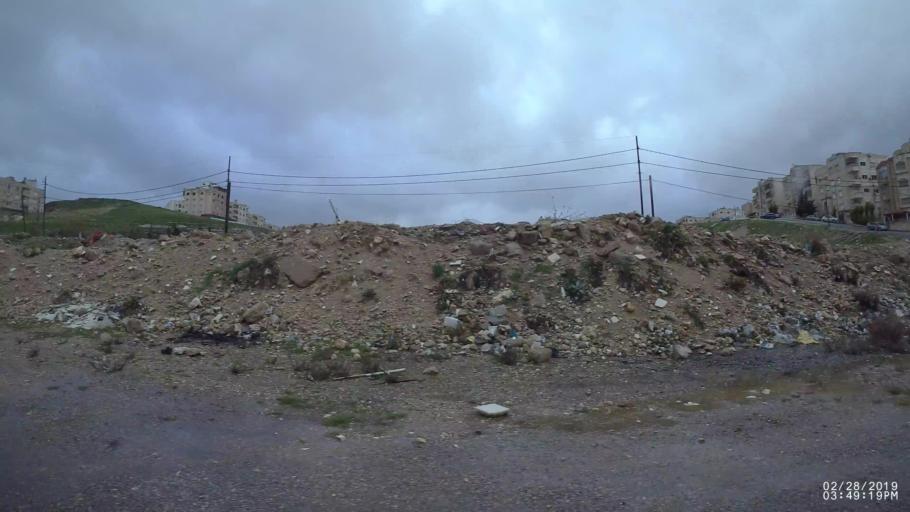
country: JO
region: Amman
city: Amman
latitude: 31.9947
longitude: 35.9245
